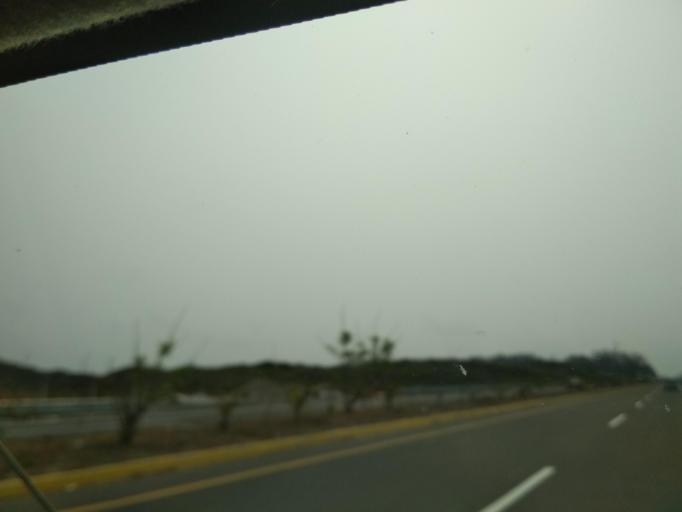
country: MX
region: Veracruz
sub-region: Alvarado
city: Playa de la Libertad
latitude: 19.0556
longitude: -96.0522
